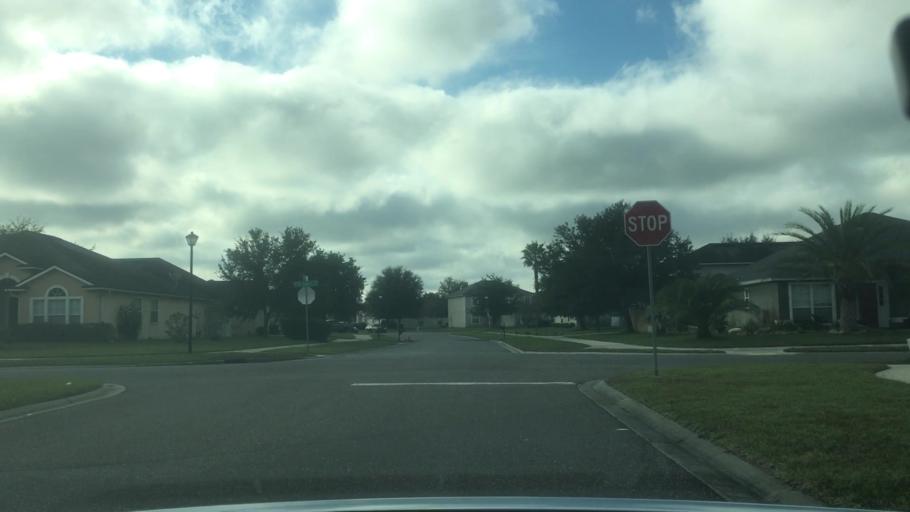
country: US
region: Florida
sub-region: Nassau County
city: Yulee
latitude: 30.4915
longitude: -81.5701
